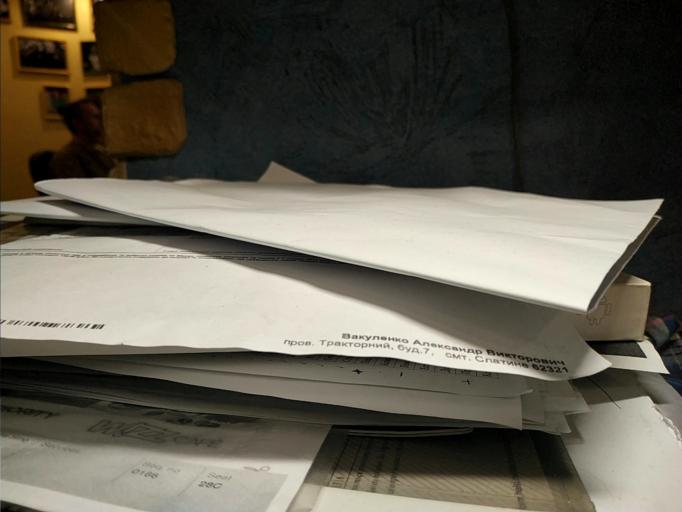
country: RU
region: Tverskaya
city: Zubtsov
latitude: 56.1239
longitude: 34.5518
